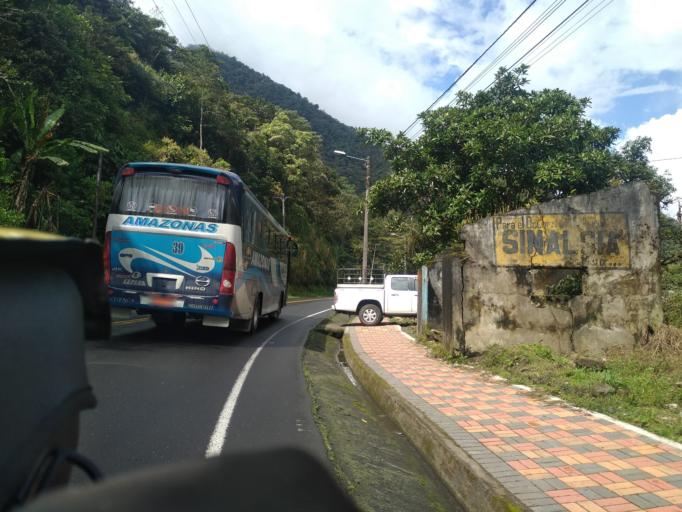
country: EC
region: Tungurahua
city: Banos
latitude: -1.4016
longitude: -78.2868
